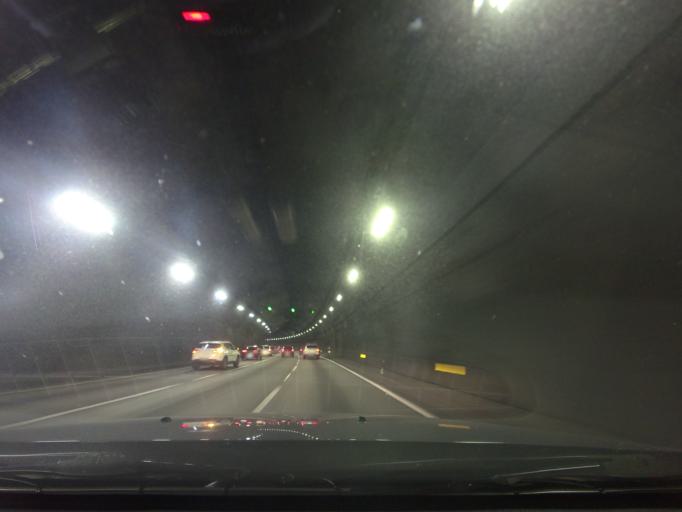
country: BR
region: Sao Paulo
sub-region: Cubatao
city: Cubatao
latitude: -23.8876
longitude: -46.5039
